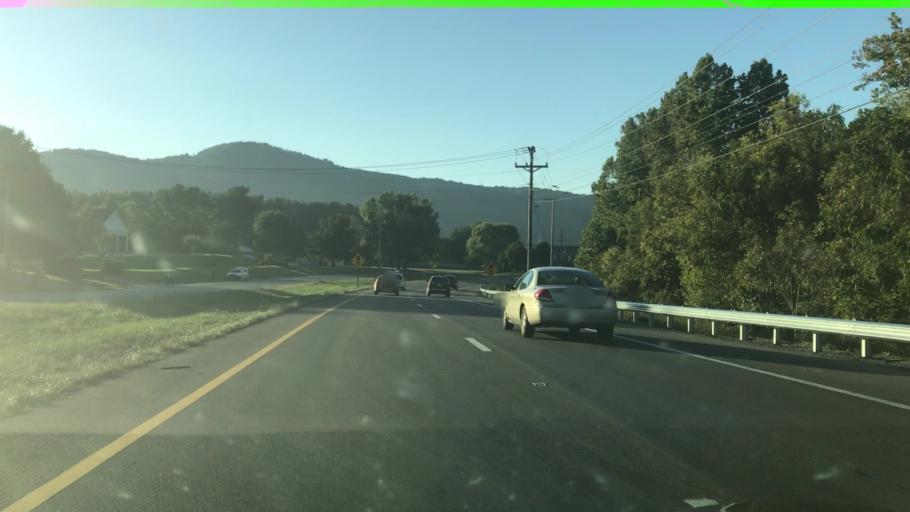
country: US
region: Virginia
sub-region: Botetourt County
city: Laymantown
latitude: 37.3328
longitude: -79.8737
